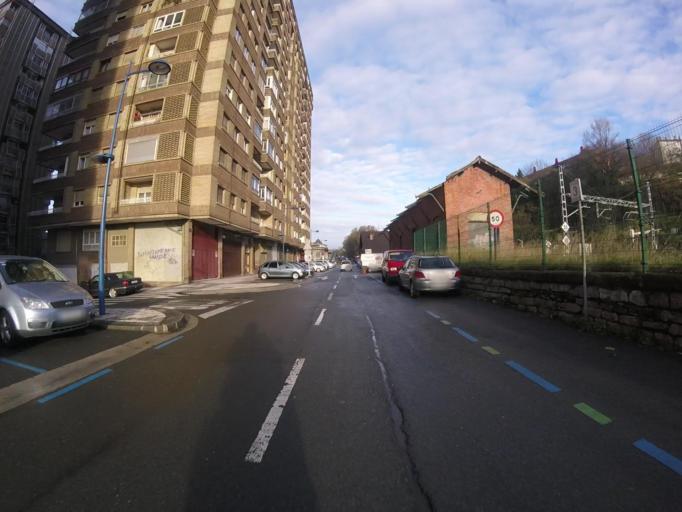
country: ES
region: Basque Country
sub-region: Provincia de Guipuzcoa
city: Errenteria
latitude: 43.3151
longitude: -1.8985
